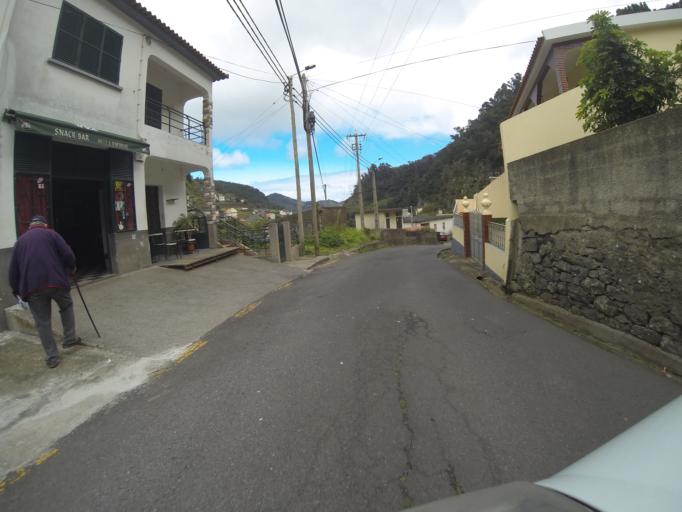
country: PT
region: Madeira
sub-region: Machico
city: Machico
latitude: 32.7352
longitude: -16.7931
